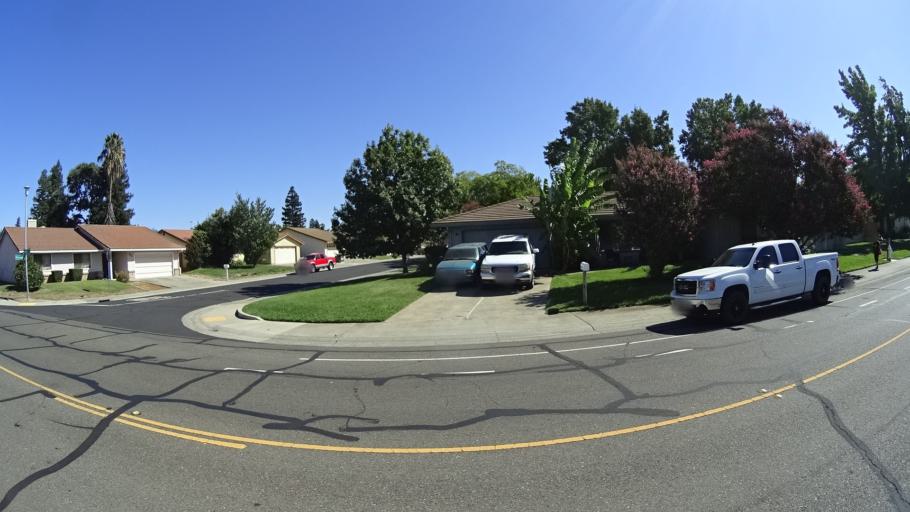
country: US
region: California
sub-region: Sacramento County
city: Elk Grove
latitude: 38.4157
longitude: -121.3835
